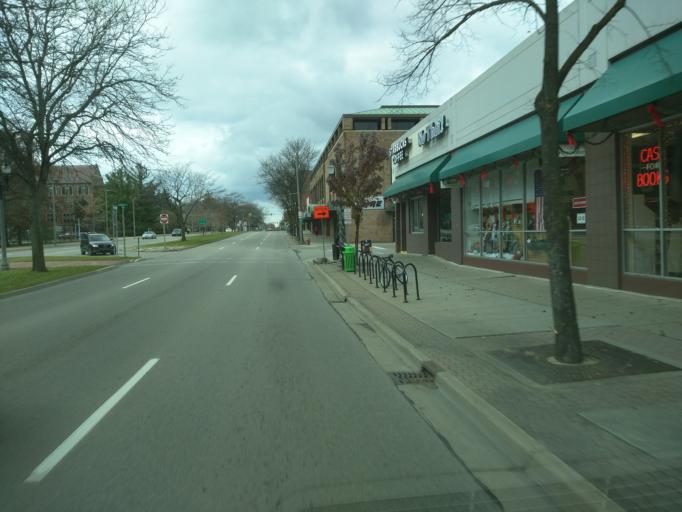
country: US
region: Michigan
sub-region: Ingham County
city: East Lansing
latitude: 42.7341
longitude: -84.4795
